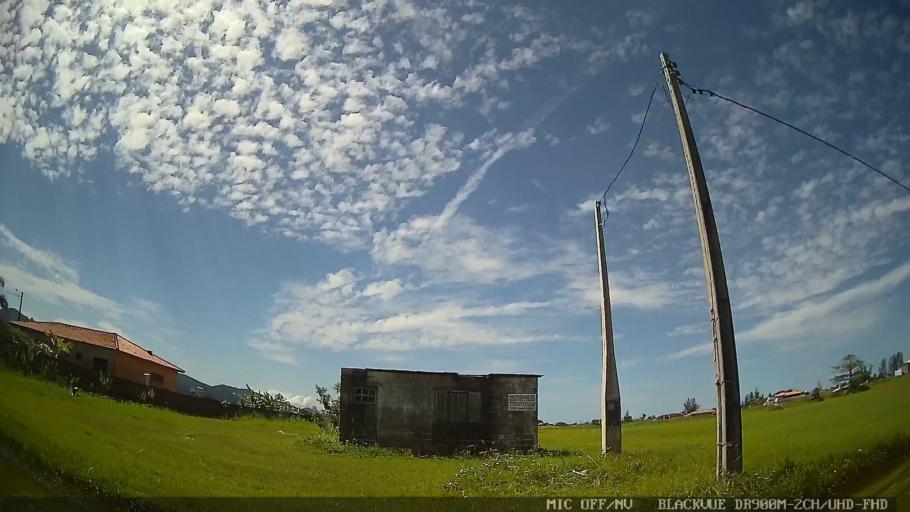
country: BR
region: Sao Paulo
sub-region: Iguape
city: Iguape
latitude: -24.7257
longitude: -47.5168
